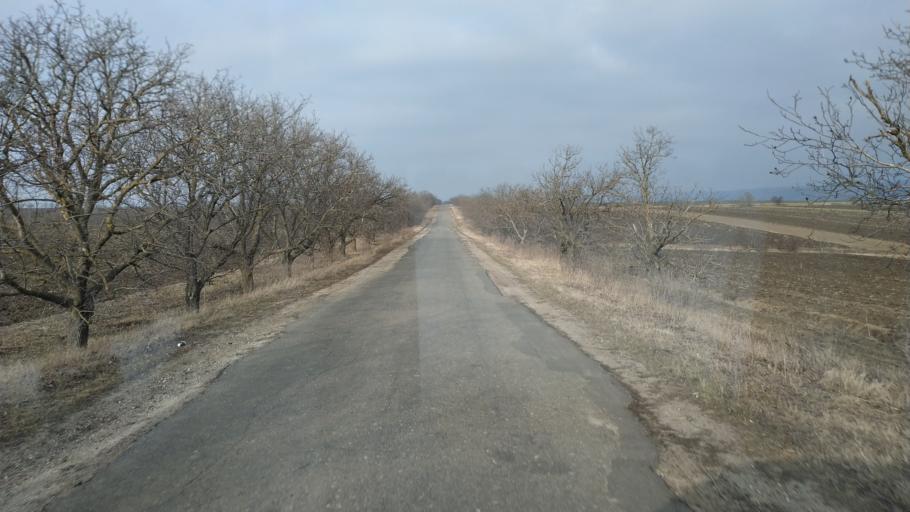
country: MD
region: Hincesti
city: Dancu
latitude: 46.8567
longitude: 28.2886
